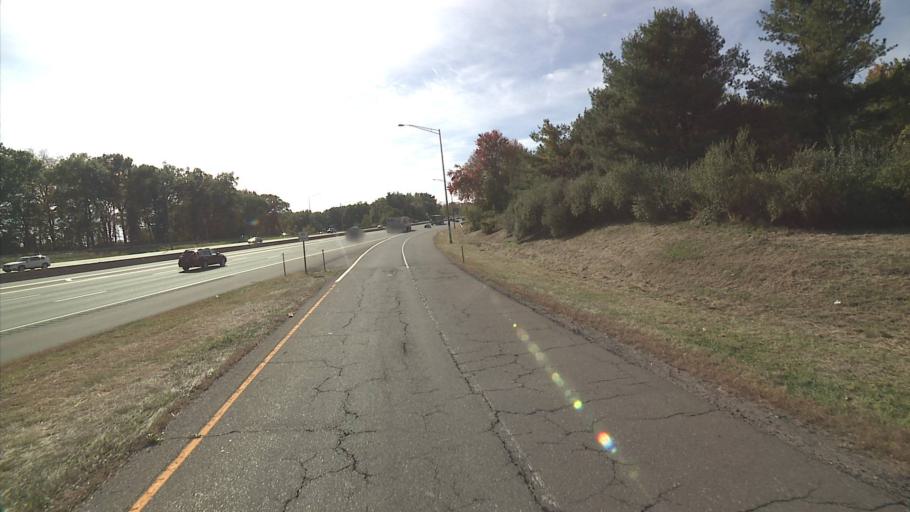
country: US
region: Connecticut
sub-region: Hartford County
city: East Hartford
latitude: 41.7760
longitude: -72.5752
